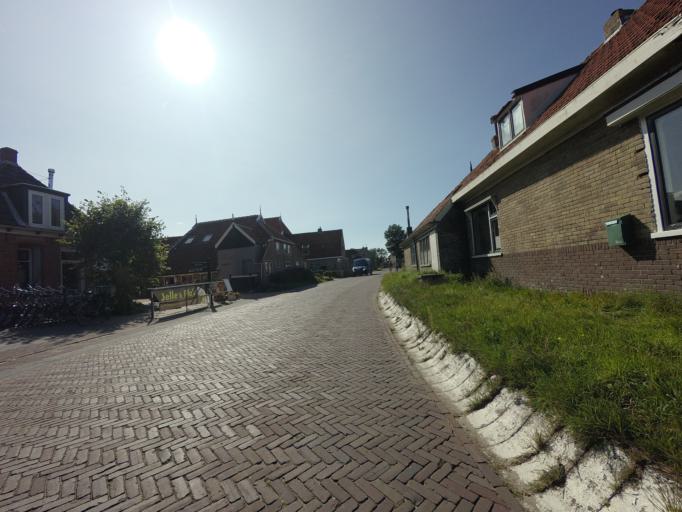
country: NL
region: Friesland
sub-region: Gemeente Terschelling
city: West-Terschelling
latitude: 53.3941
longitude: 5.3279
